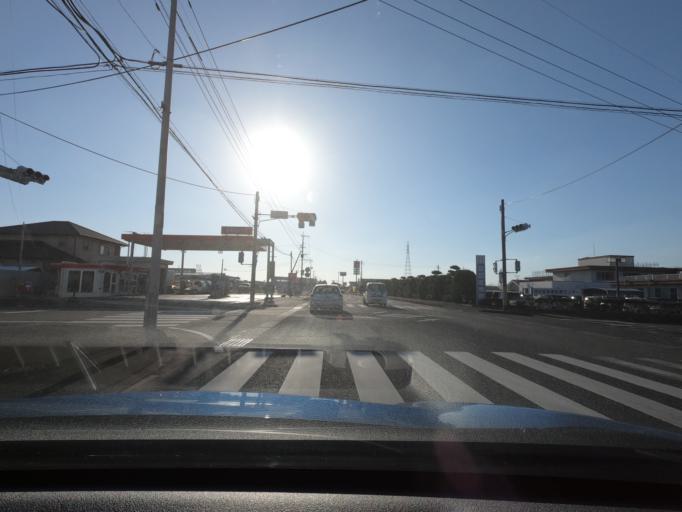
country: JP
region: Kagoshima
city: Izumi
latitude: 32.0888
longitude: 130.2866
